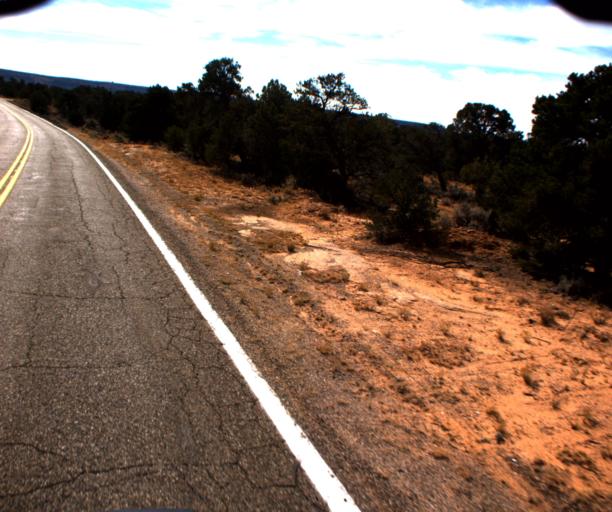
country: US
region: Arizona
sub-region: Navajo County
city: Kayenta
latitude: 36.5922
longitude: -110.4961
